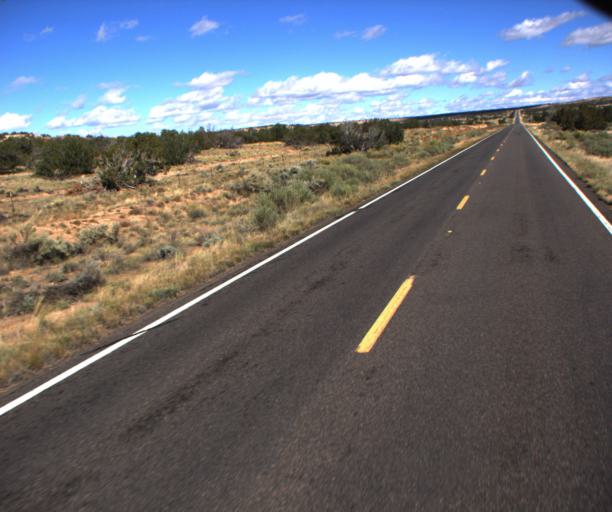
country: US
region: Arizona
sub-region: Apache County
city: Saint Johns
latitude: 34.7890
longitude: -109.2382
